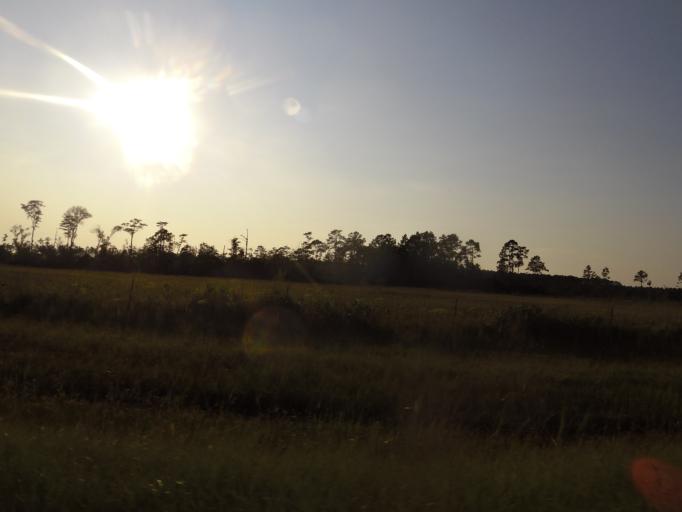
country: US
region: Florida
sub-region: Nassau County
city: Callahan
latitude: 30.5325
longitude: -81.9895
